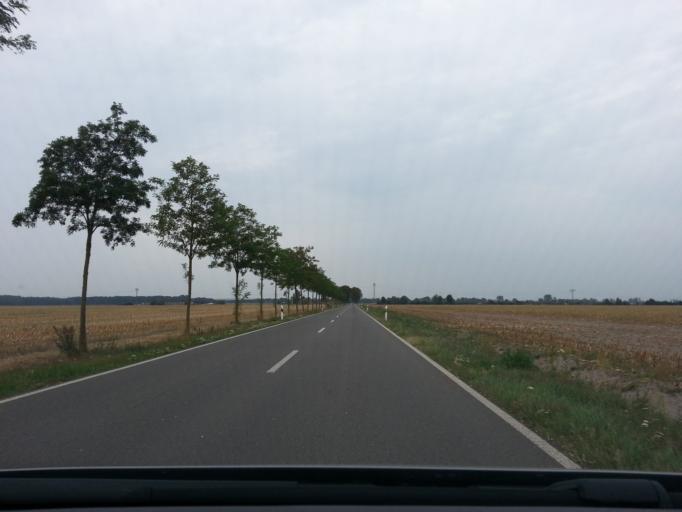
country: DE
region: Mecklenburg-Vorpommern
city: Ferdinandshof
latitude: 53.6972
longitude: 13.9299
